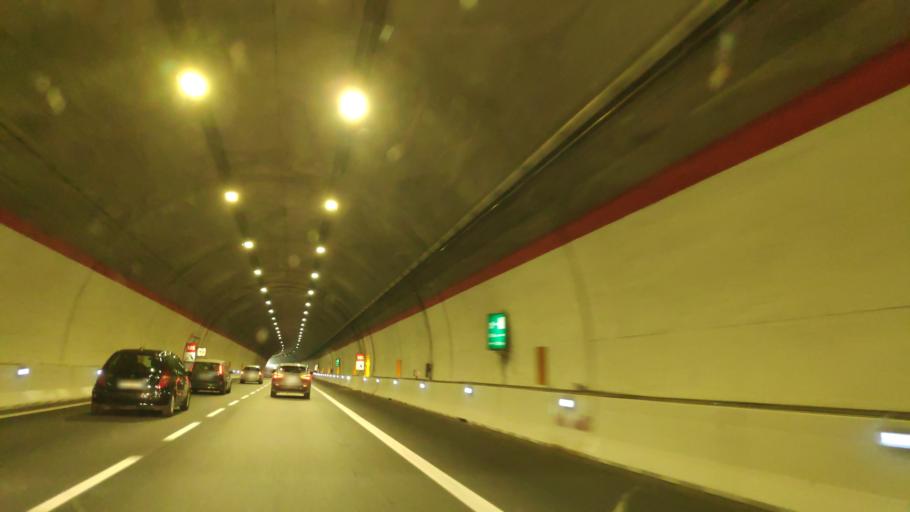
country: IT
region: Campania
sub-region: Provincia di Salerno
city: Sicignano degli Alburni
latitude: 40.5797
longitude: 15.3441
